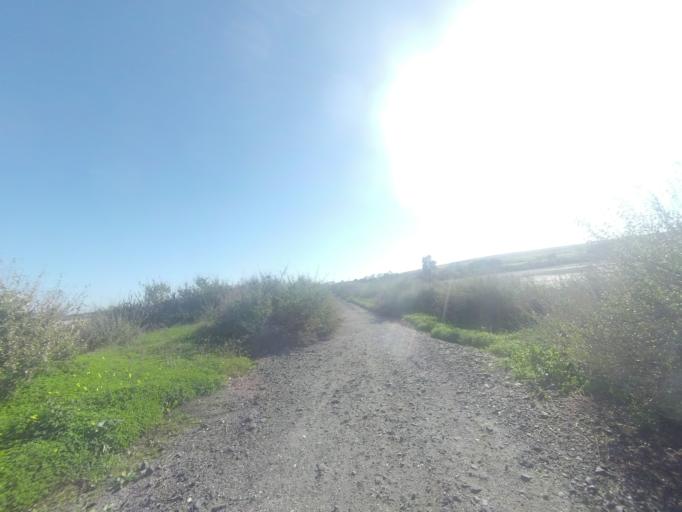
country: ES
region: Andalusia
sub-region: Provincia de Huelva
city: Huelva
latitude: 37.2581
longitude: -6.9168
